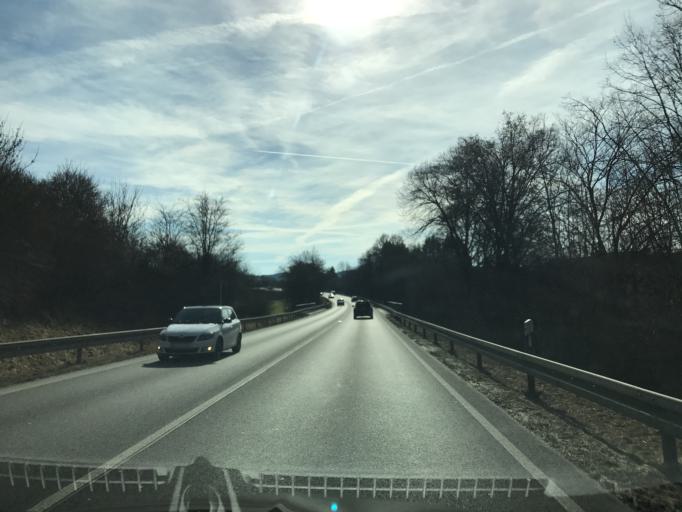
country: DE
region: Baden-Wuerttemberg
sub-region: Tuebingen Region
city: Hochdorf
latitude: 48.0057
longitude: 9.7730
